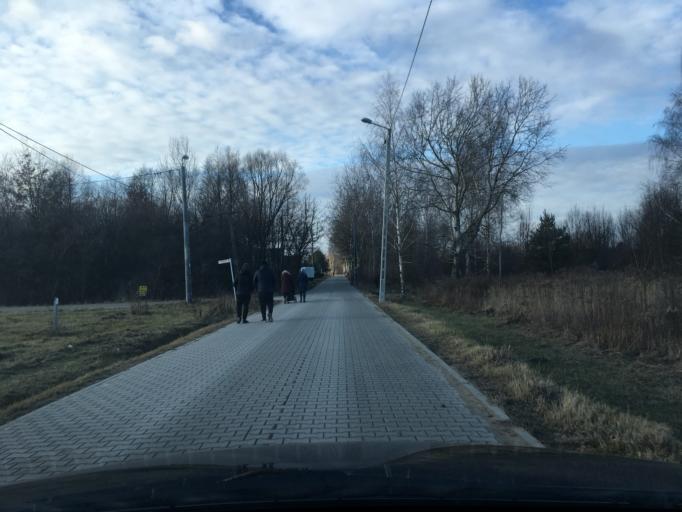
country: PL
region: Masovian Voivodeship
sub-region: Powiat piaseczynski
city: Lesznowola
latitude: 52.0268
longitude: 20.9411
